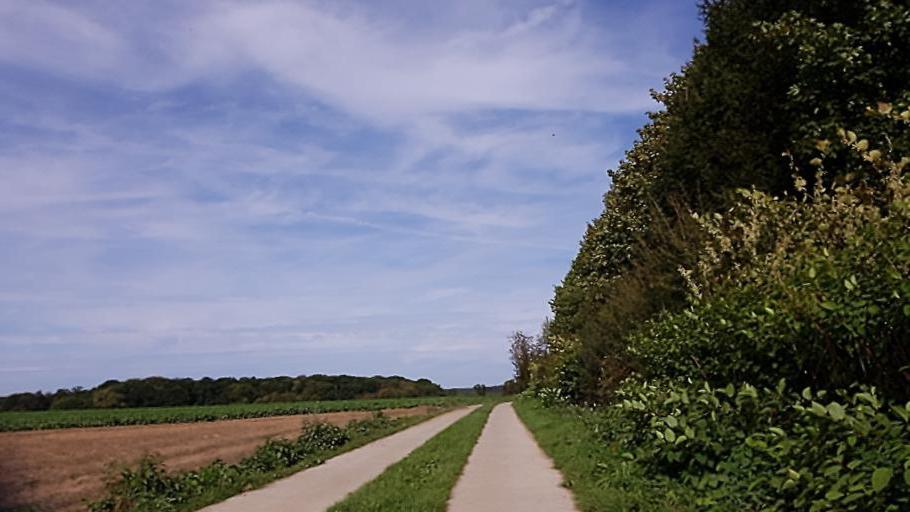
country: BE
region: Wallonia
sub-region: Province du Brabant Wallon
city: Grez-Doiceau
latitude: 50.7713
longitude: 4.6852
